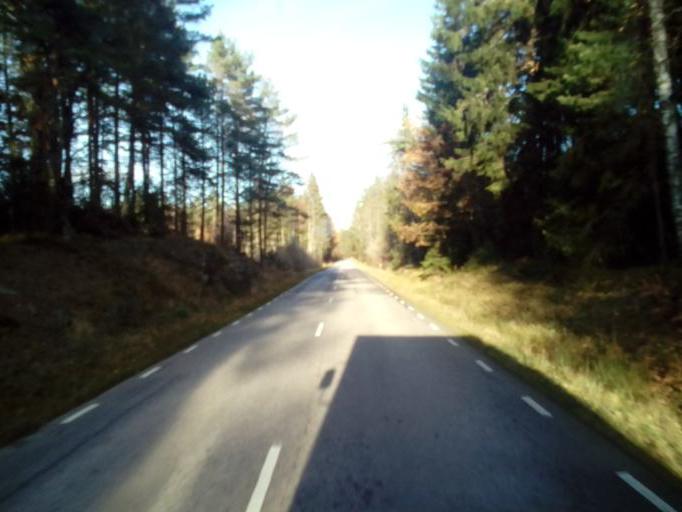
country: SE
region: Kalmar
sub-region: Vasterviks Kommun
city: Ankarsrum
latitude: 57.7512
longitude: 16.1173
